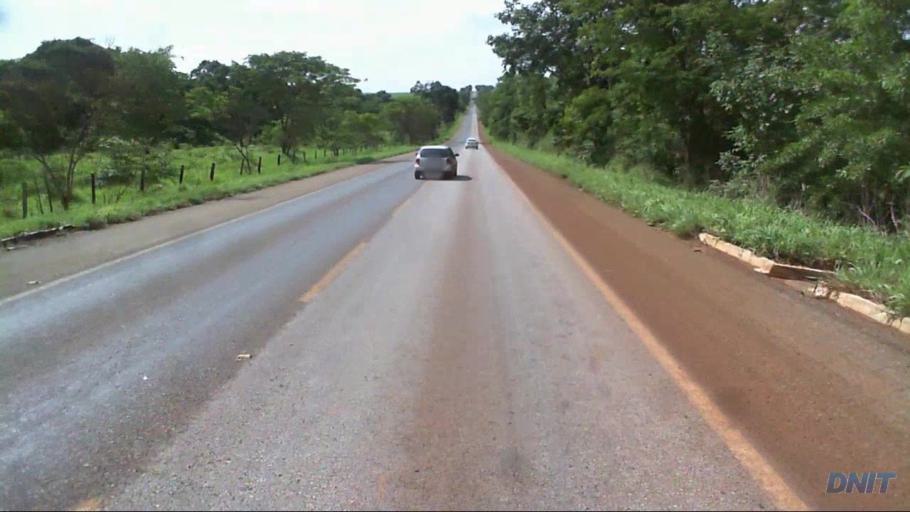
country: BR
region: Goias
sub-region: Barro Alto
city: Barro Alto
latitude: -15.0066
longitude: -48.9026
